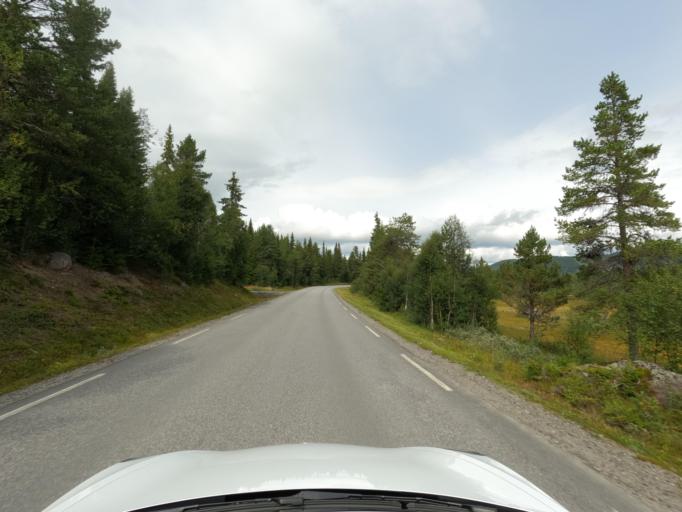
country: NO
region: Telemark
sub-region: Vinje
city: Amot
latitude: 59.7023
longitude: 8.1089
